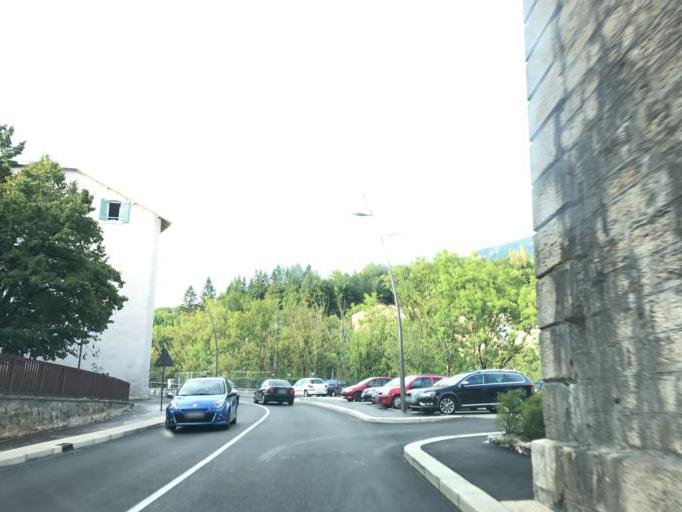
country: FR
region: Rhone-Alpes
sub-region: Departement de l'Ain
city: Bellegarde-sur-Valserine
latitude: 46.1100
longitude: 5.8282
